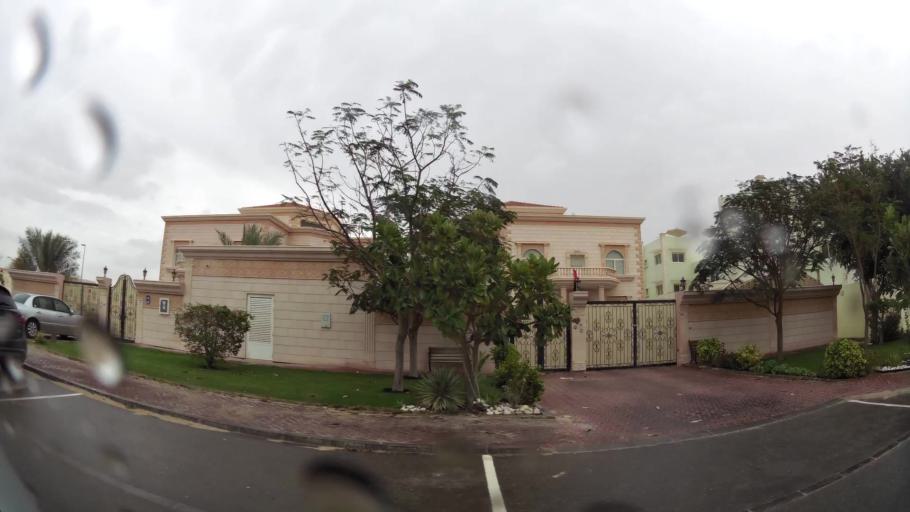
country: AE
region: Abu Dhabi
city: Abu Dhabi
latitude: 24.3647
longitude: 54.6429
